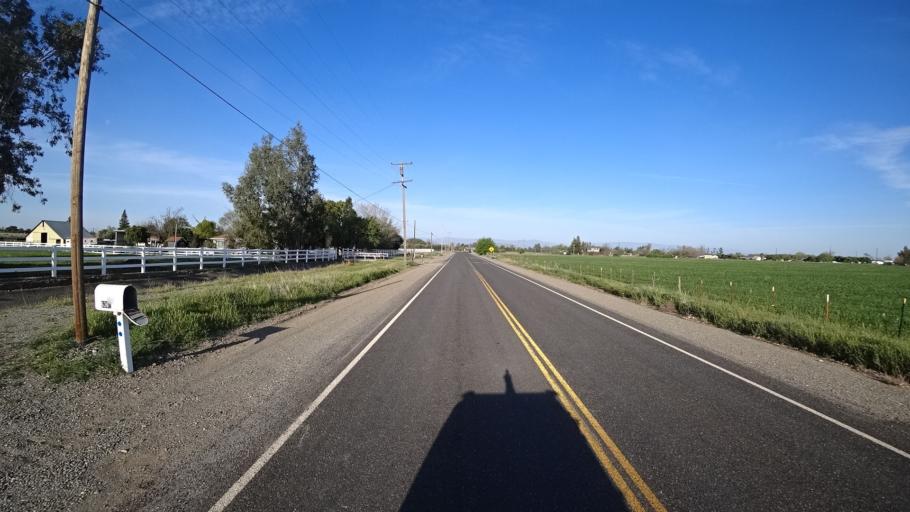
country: US
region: California
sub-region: Glenn County
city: Orland
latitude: 39.7403
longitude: -122.2128
